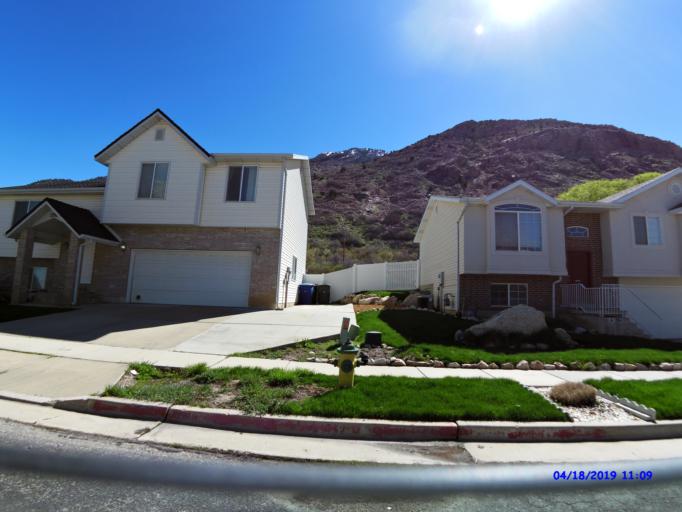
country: US
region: Utah
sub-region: Weber County
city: North Ogden
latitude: 41.2822
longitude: -111.9498
